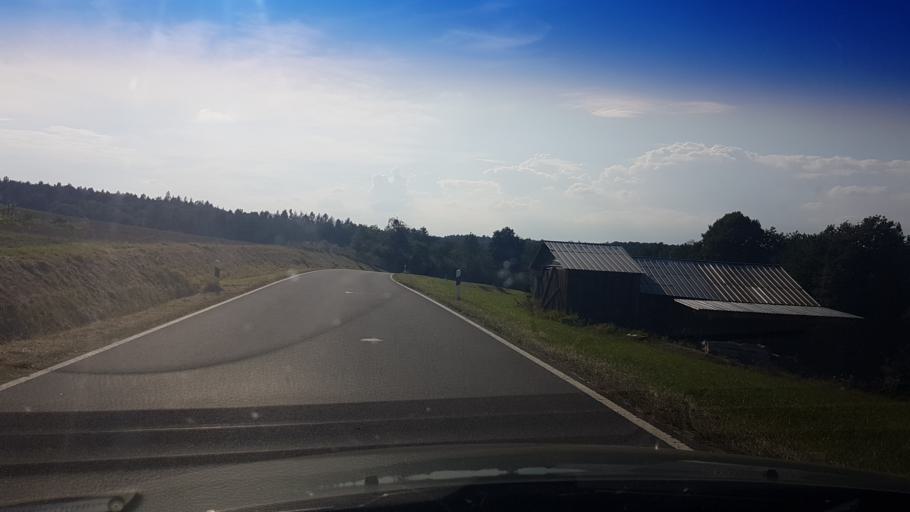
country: DE
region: Bavaria
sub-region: Upper Franconia
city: Zapfendorf
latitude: 50.0140
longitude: 10.9733
